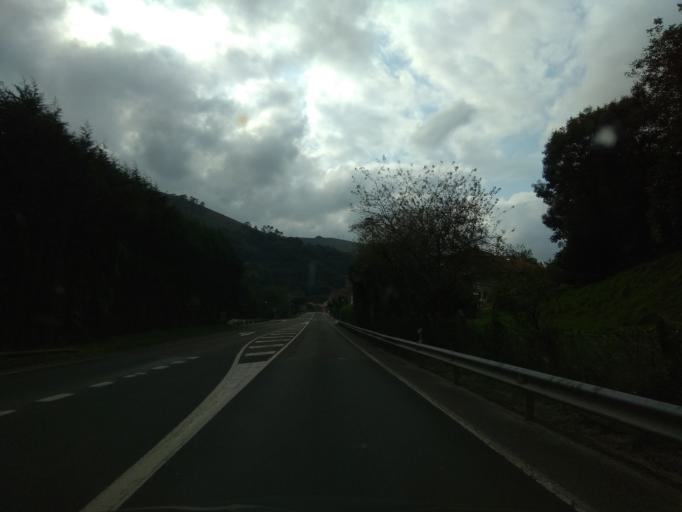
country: ES
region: Cantabria
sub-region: Provincia de Cantabria
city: Cabezon de la Sal
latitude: 43.3171
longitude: -4.2983
